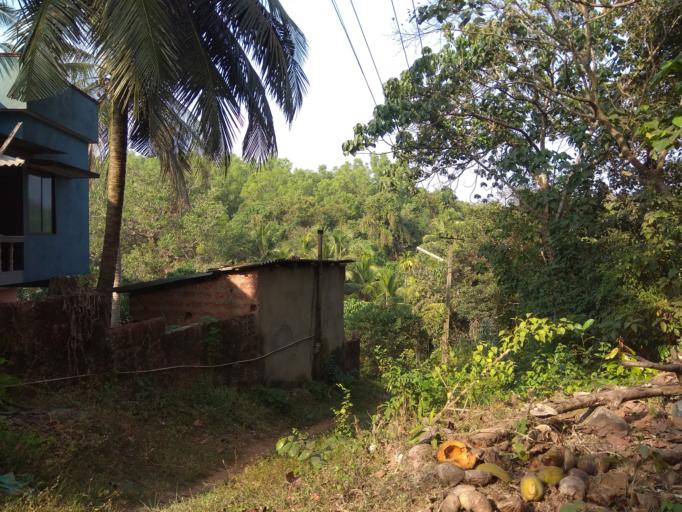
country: IN
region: Karnataka
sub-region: Dakshina Kannada
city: Mangalore
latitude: 12.9236
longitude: 74.8730
